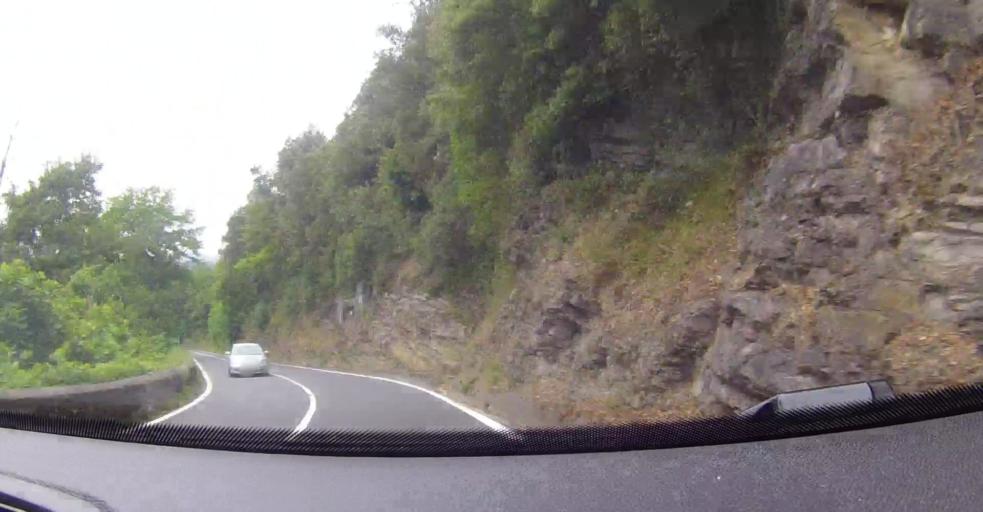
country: ES
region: Basque Country
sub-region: Bizkaia
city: Lanestosa
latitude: 43.2419
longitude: -3.3605
